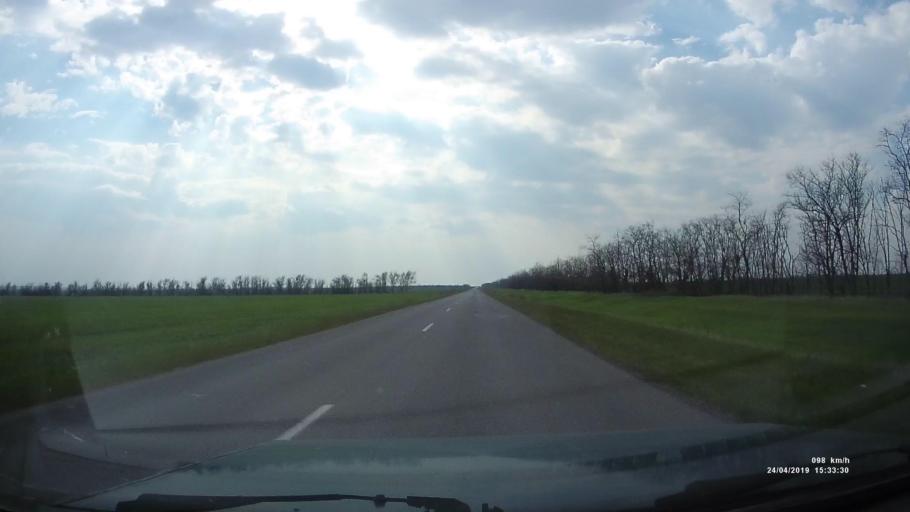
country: RU
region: Kalmykiya
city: Yashalta
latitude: 46.6003
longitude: 42.9365
